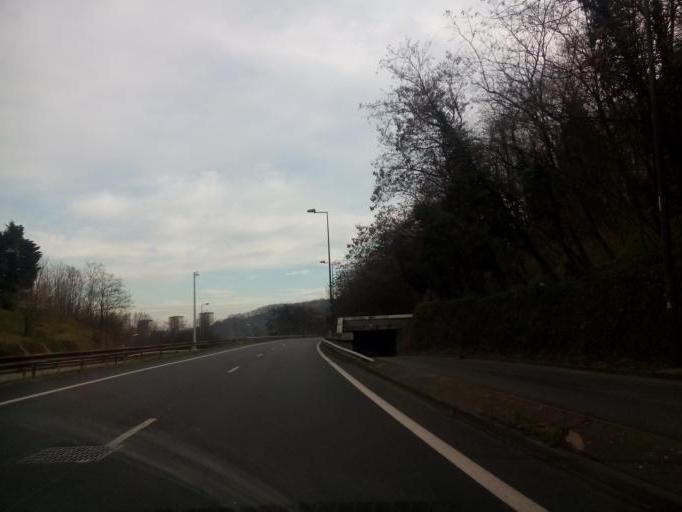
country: FR
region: Rhone-Alpes
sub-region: Departement du Rhone
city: Tassin-la-Demi-Lune
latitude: 45.7660
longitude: 4.7905
